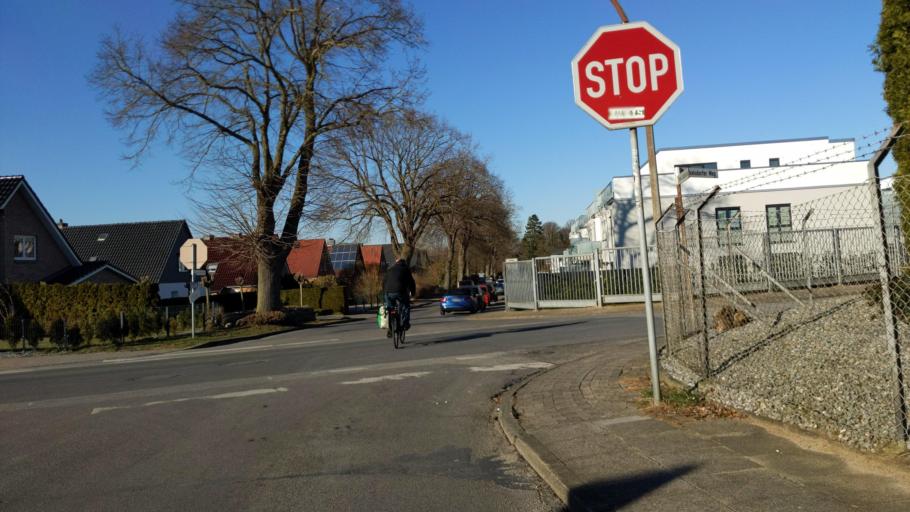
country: DE
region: Schleswig-Holstein
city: Stockelsdorf
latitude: 53.9095
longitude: 10.6671
